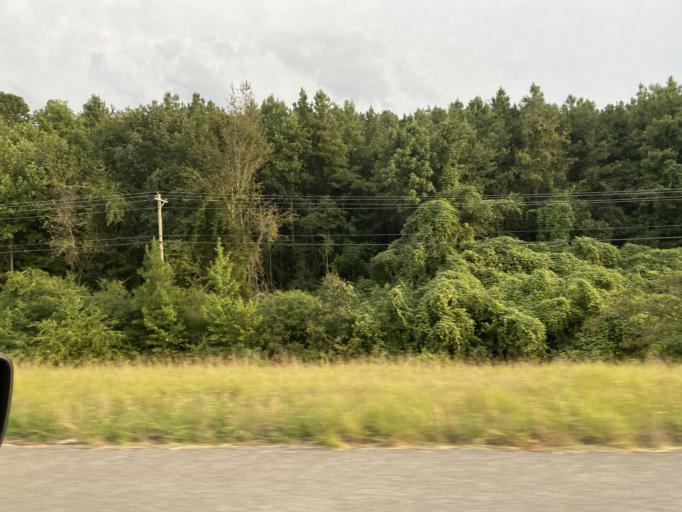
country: US
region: Alabama
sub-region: Franklin County
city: Red Bay
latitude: 34.4492
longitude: -88.0723
